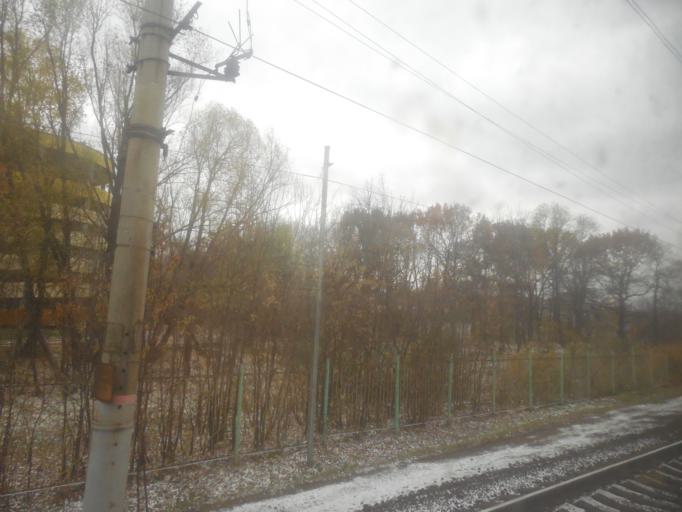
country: RU
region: Moskovskaya
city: Bol'shaya Setun'
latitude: 55.7271
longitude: 37.4123
